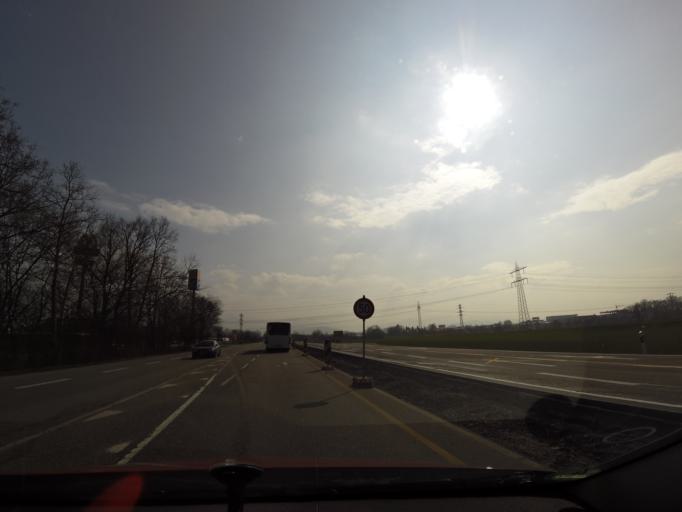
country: DE
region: Baden-Wuerttemberg
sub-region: Freiburg Region
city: Achern
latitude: 48.6413
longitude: 8.0354
